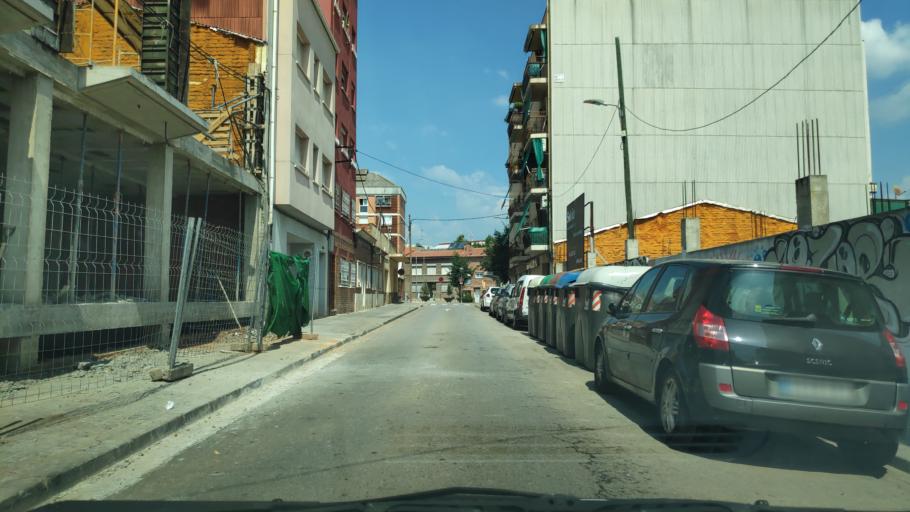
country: ES
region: Catalonia
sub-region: Provincia de Barcelona
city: Sant Quirze del Valles
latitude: 41.5499
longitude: 2.0854
